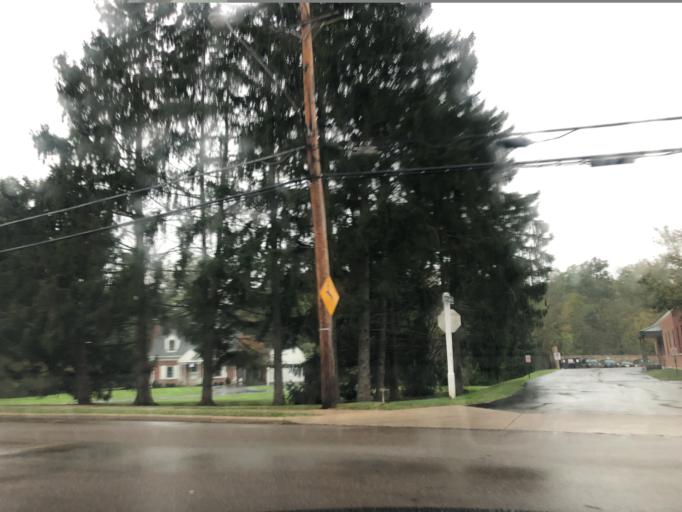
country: US
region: Ohio
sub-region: Hamilton County
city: Loveland
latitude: 39.2699
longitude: -84.2840
